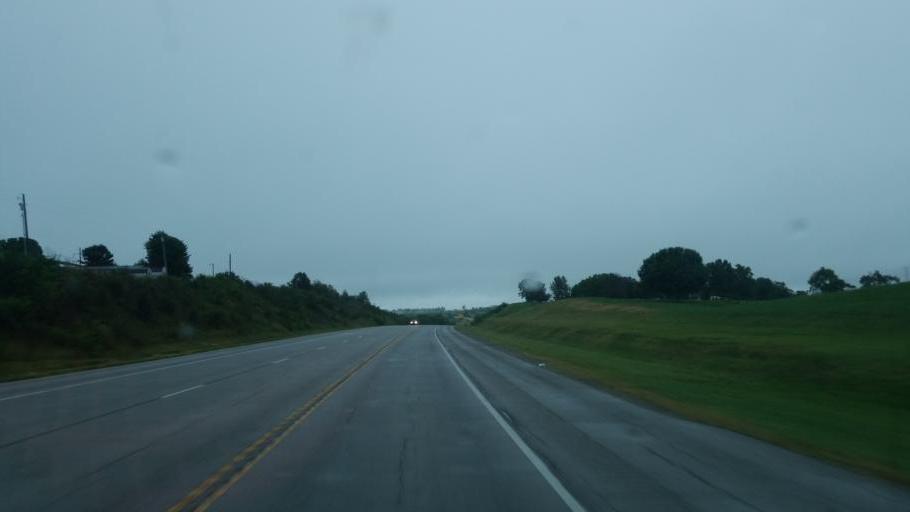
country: US
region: Kentucky
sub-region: Fleming County
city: Flemingsburg
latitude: 38.4077
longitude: -83.7309
